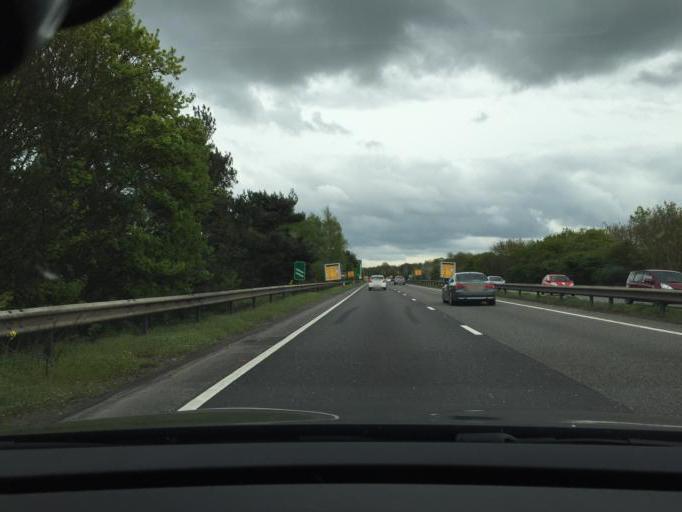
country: GB
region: England
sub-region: Oxfordshire
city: Harwell
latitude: 51.6238
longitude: -1.3069
